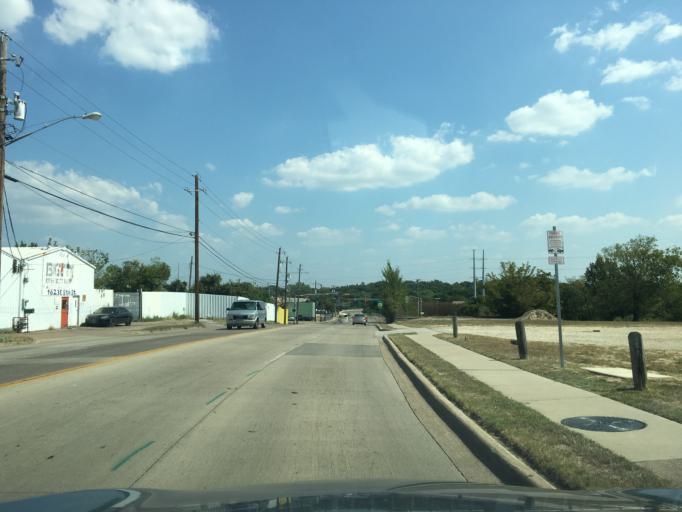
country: US
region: Texas
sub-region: Dallas County
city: Dallas
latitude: 32.7498
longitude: -96.8004
